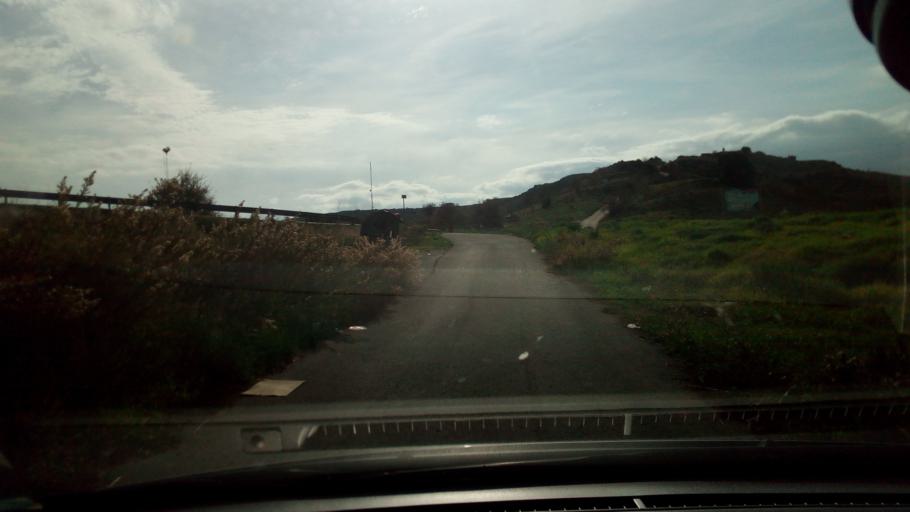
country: CY
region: Pafos
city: Mesogi
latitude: 34.7932
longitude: 32.4806
